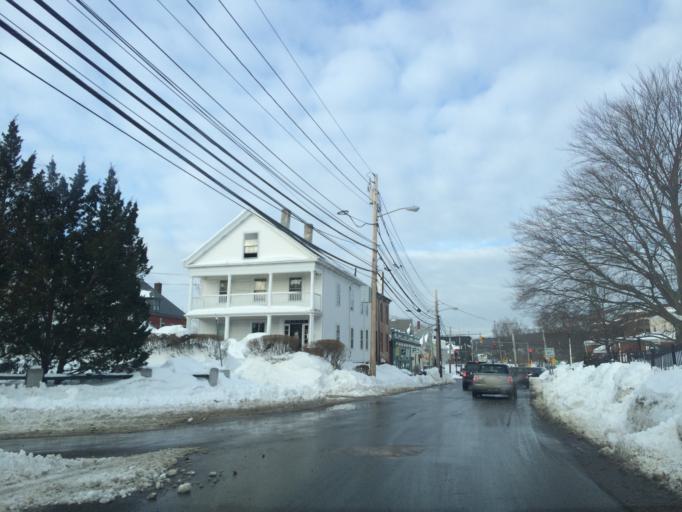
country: US
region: Massachusetts
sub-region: Middlesex County
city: Waltham
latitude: 42.3779
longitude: -71.2345
